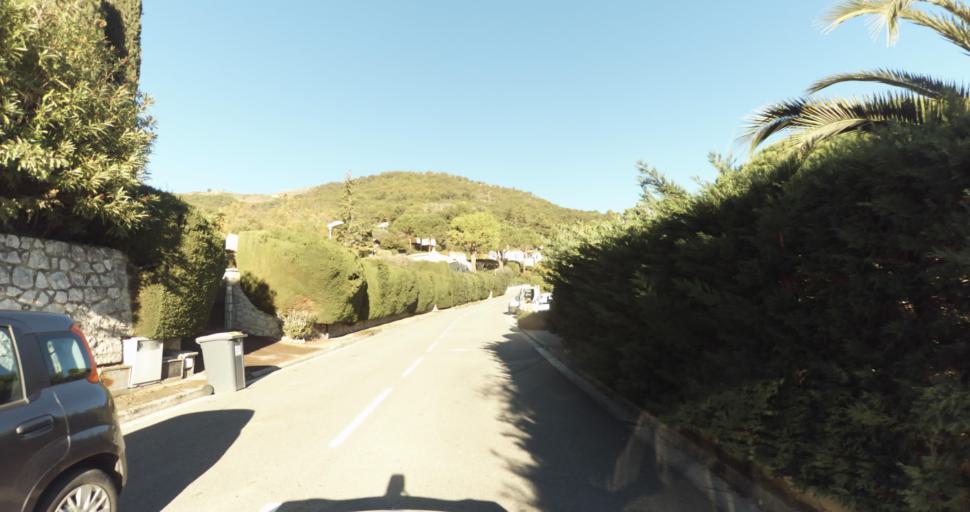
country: FR
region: Provence-Alpes-Cote d'Azur
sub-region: Departement des Alpes-Maritimes
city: Vence
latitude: 43.7247
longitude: 7.0826
